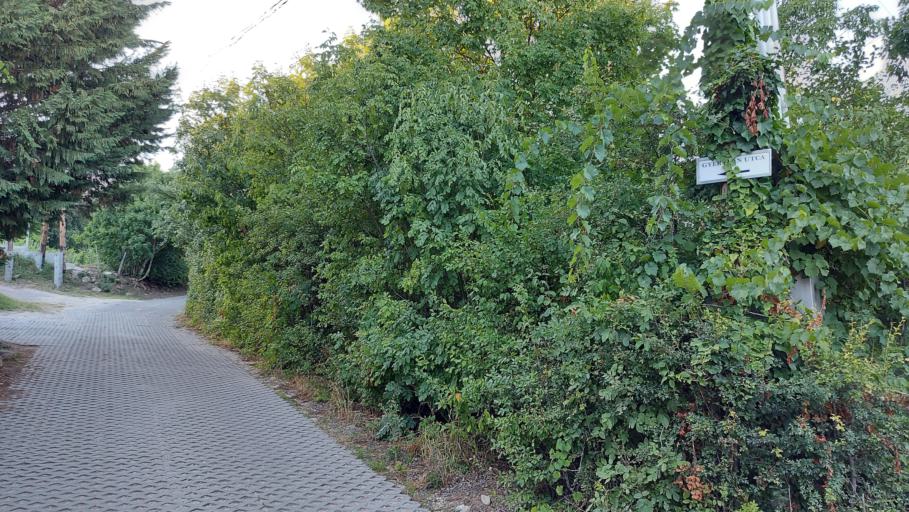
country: HU
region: Veszprem
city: Balatonalmadi
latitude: 47.0581
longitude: 18.0100
